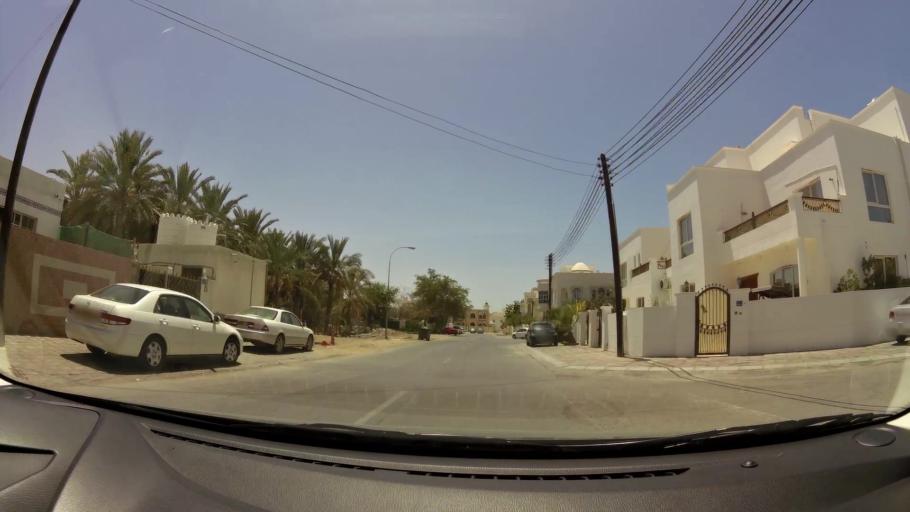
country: OM
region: Muhafazat Masqat
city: Bawshar
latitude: 23.5978
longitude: 58.3818
